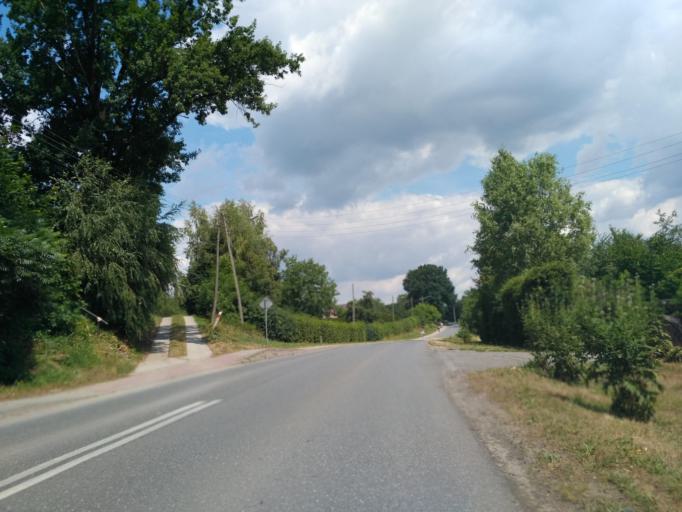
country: PL
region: Subcarpathian Voivodeship
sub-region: Powiat debicki
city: Pilzno
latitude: 49.9826
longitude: 21.2874
